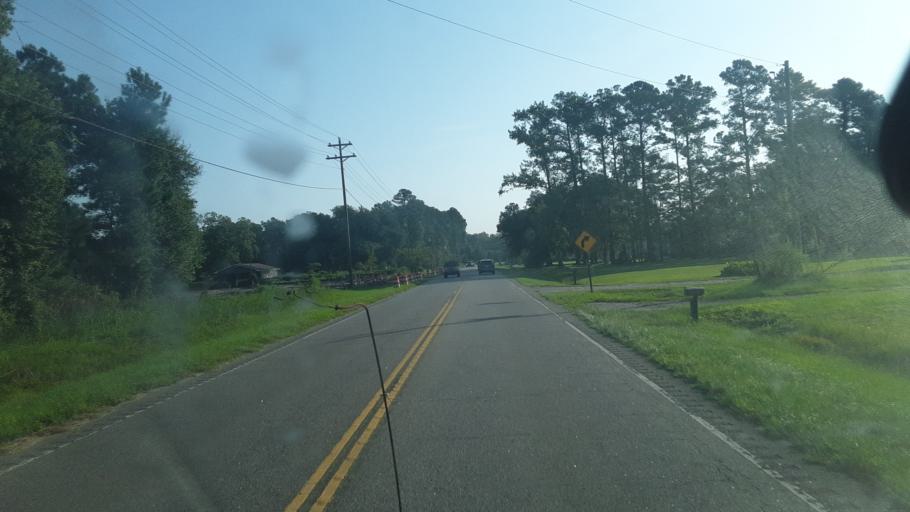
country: US
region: South Carolina
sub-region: Horry County
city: Forestbrook
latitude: 33.8271
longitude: -78.8960
